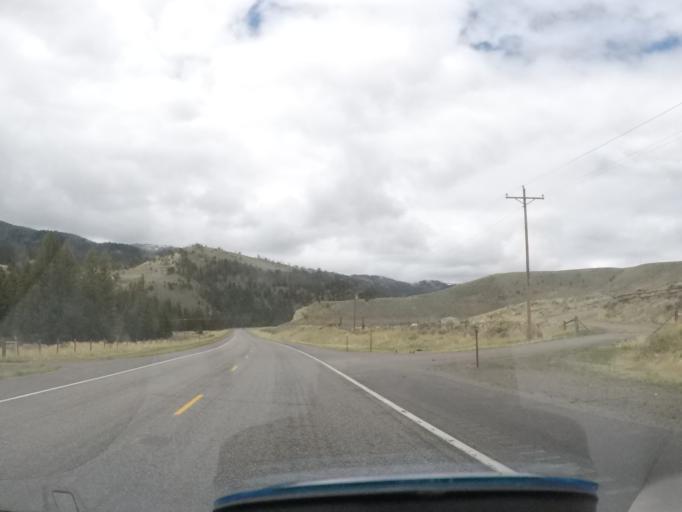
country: US
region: Wyoming
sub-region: Sublette County
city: Pinedale
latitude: 43.5793
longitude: -109.7507
